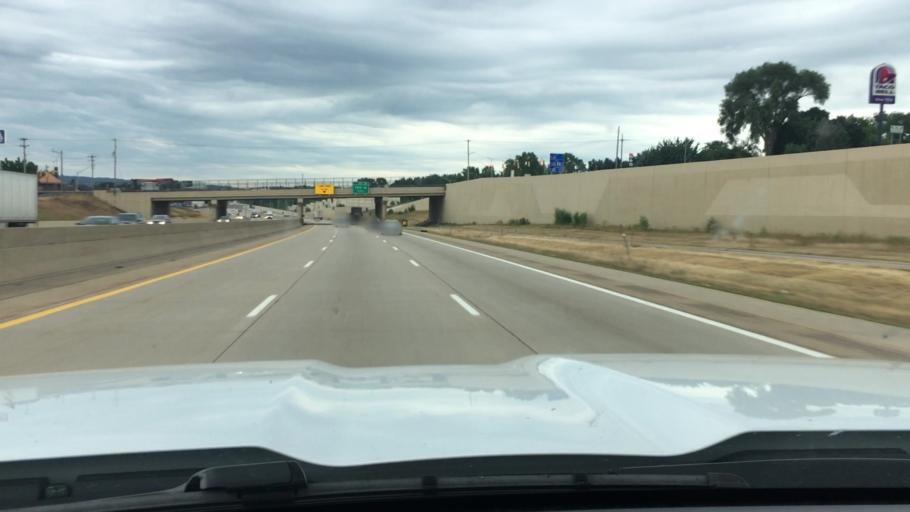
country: US
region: Michigan
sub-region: Kent County
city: Cutlerville
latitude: 42.8428
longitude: -85.6784
